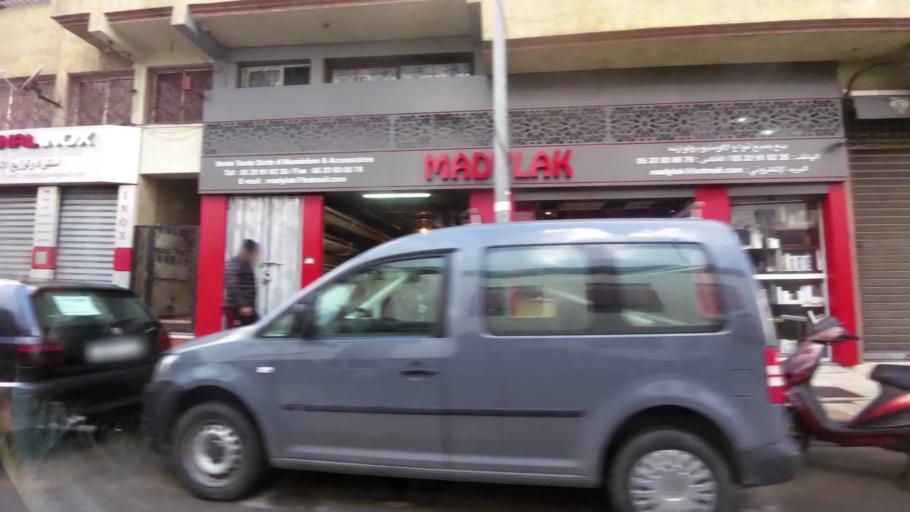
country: MA
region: Grand Casablanca
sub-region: Casablanca
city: Casablanca
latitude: 33.5394
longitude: -7.6821
